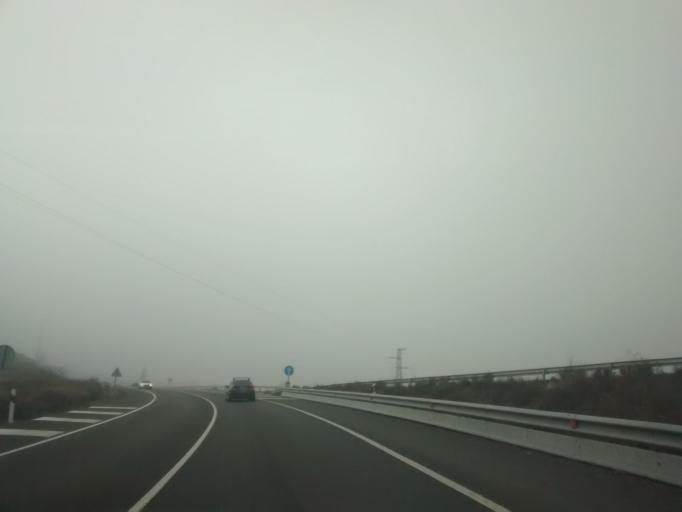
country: ES
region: La Rioja
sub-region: Provincia de La Rioja
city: Agoncillo
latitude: 42.4495
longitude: -2.3181
